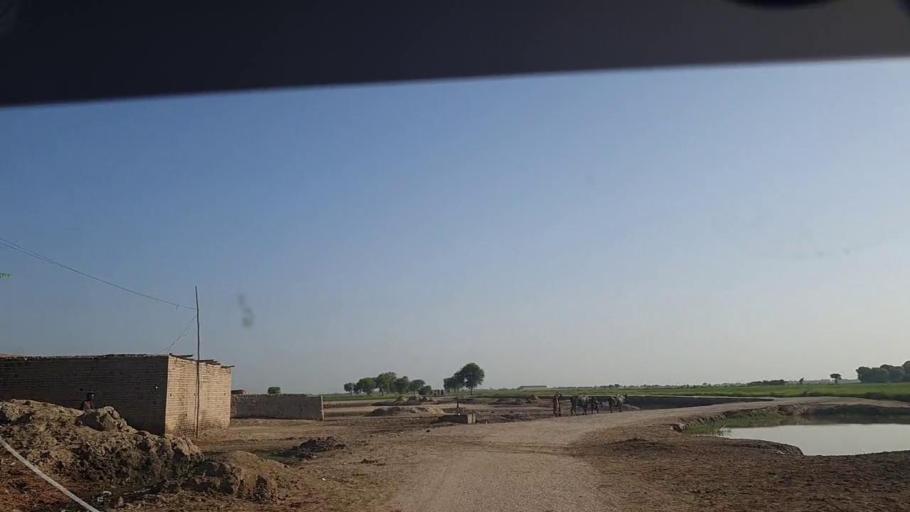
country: PK
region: Sindh
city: Tangwani
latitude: 28.2629
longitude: 69.0138
